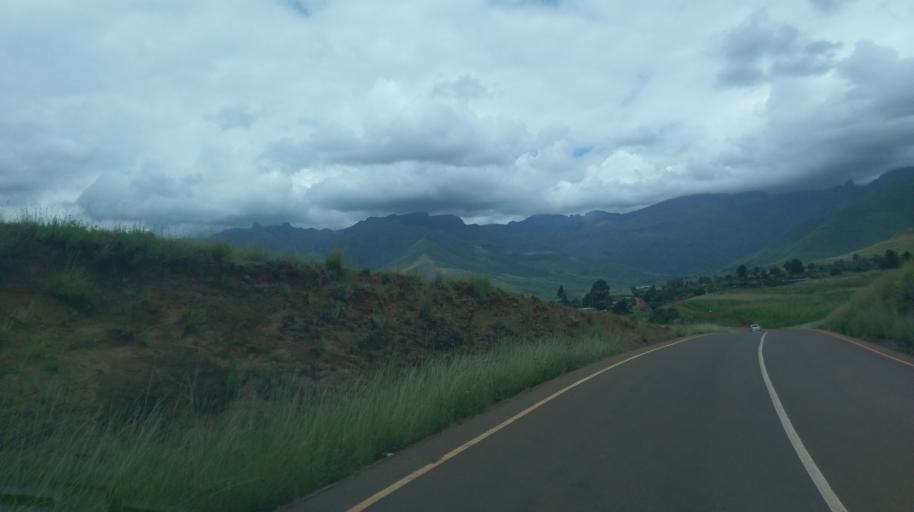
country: LS
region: Leribe
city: Leribe
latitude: -29.0362
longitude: 28.2396
